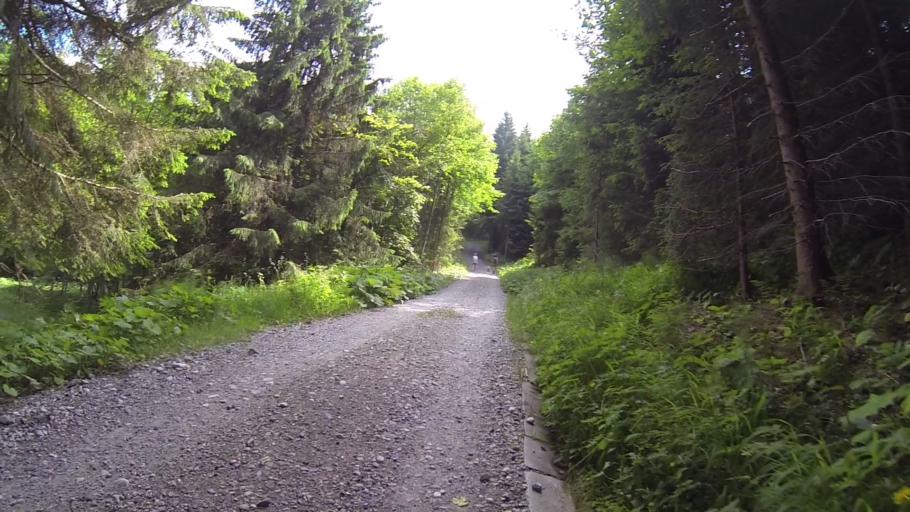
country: AT
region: Tyrol
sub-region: Politischer Bezirk Reutte
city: Jungholz
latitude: 47.5948
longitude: 10.4727
